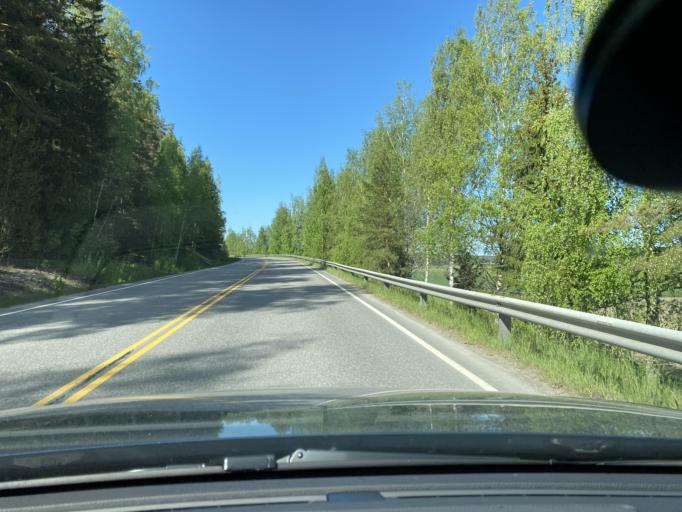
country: FI
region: Varsinais-Suomi
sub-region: Turku
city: Sauvo
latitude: 60.3579
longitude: 22.6703
